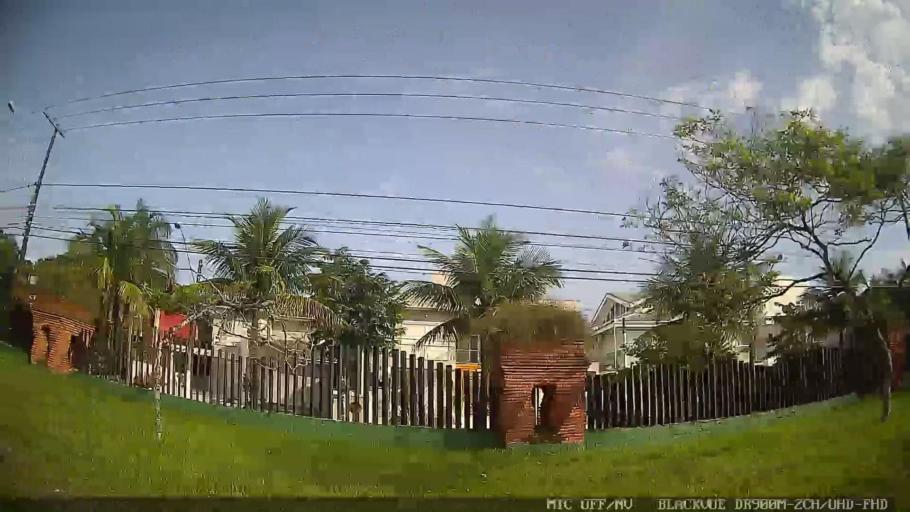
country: BR
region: Sao Paulo
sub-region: Bertioga
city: Bertioga
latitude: -23.8131
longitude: -46.0745
